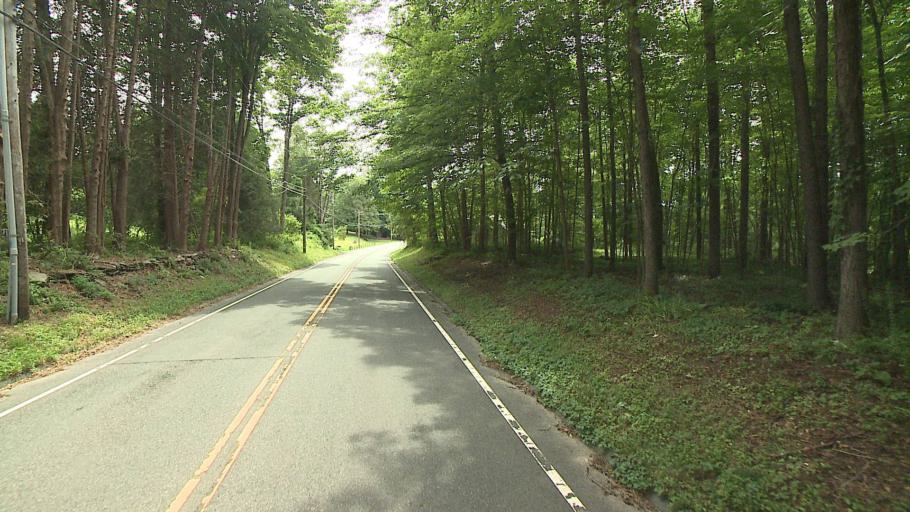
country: US
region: Connecticut
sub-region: Litchfield County
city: New Milford
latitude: 41.5711
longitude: -73.3169
